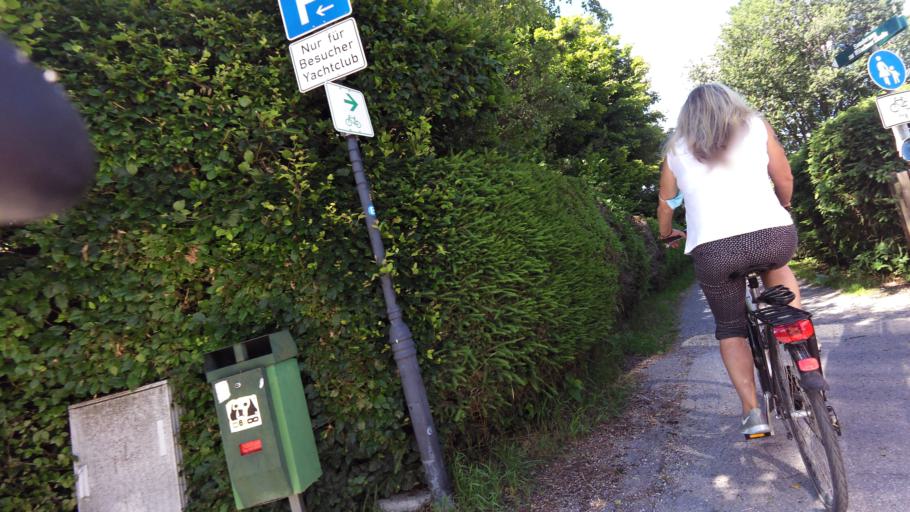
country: DE
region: Bavaria
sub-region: Upper Bavaria
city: Bad Wiessee
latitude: 47.7221
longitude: 11.7248
